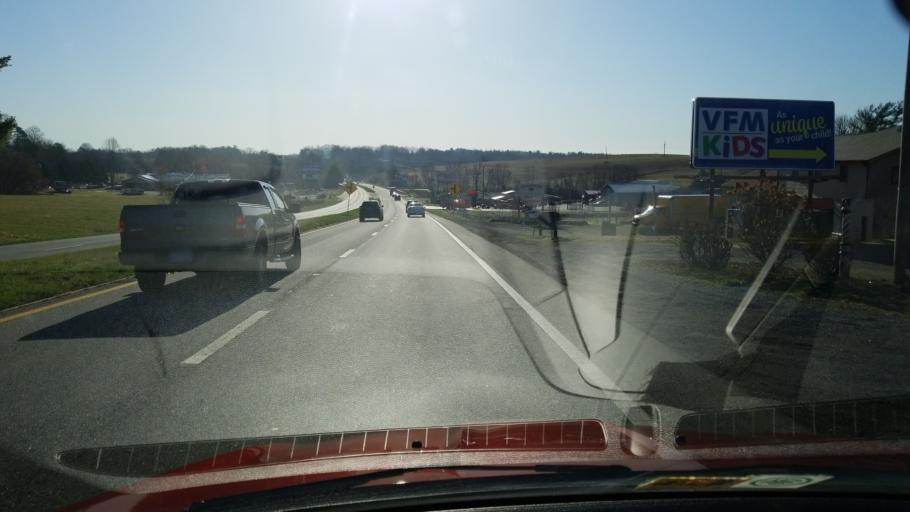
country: US
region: Virginia
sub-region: Franklin County
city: Rocky Mount
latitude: 37.0767
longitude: -79.9150
